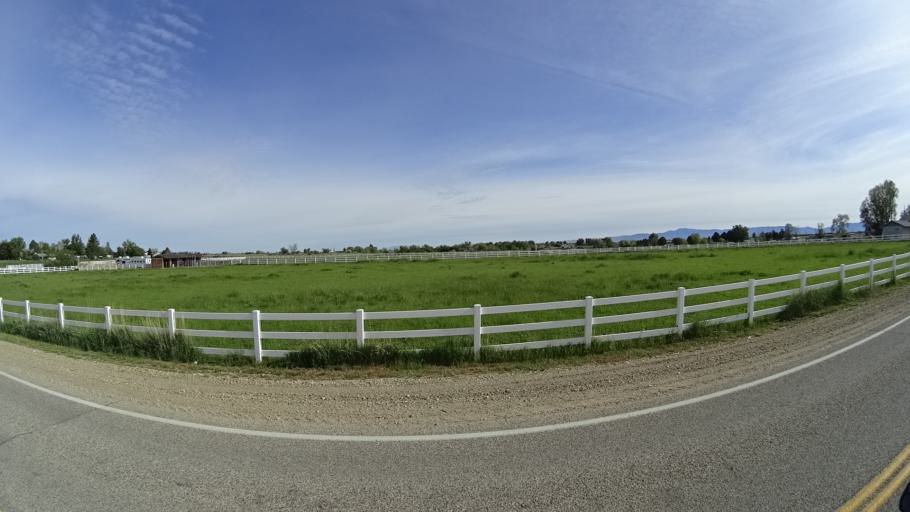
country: US
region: Idaho
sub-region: Ada County
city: Kuna
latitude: 43.4736
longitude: -116.3587
